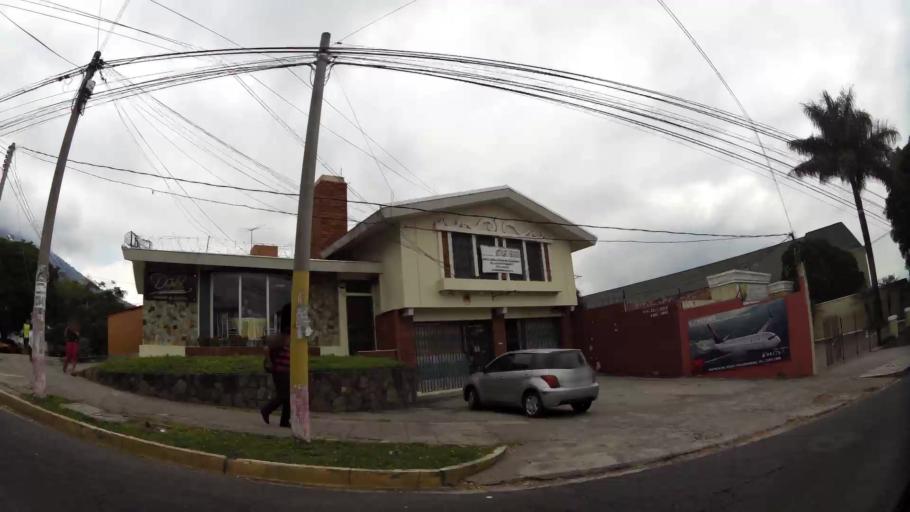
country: SV
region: San Salvador
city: Mejicanos
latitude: 13.7106
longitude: -89.2456
